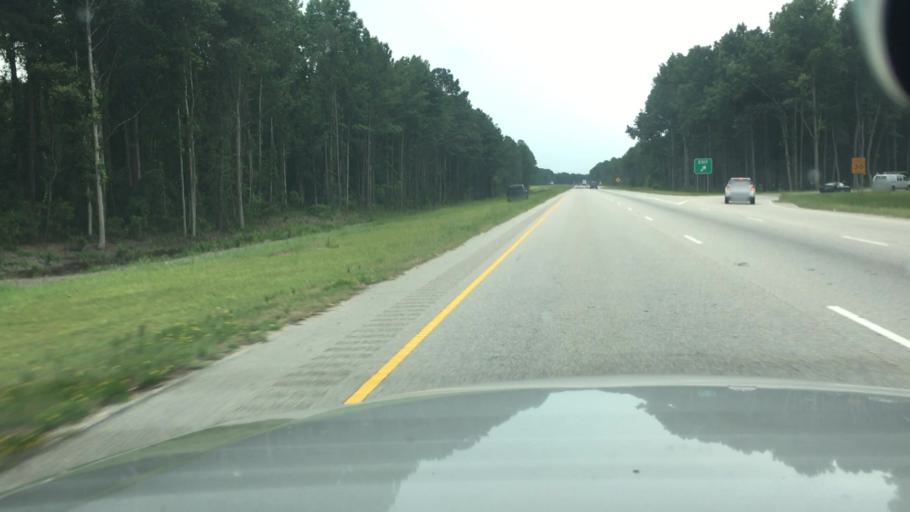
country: US
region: North Carolina
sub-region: Cumberland County
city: Fayetteville
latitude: 34.9758
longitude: -78.8564
